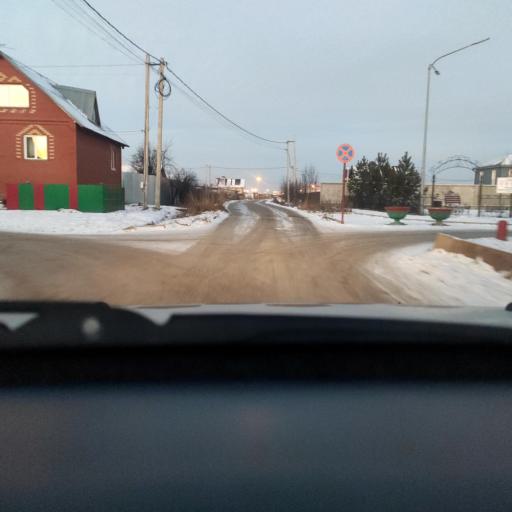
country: RU
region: Perm
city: Froly
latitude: 57.8913
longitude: 56.2567
